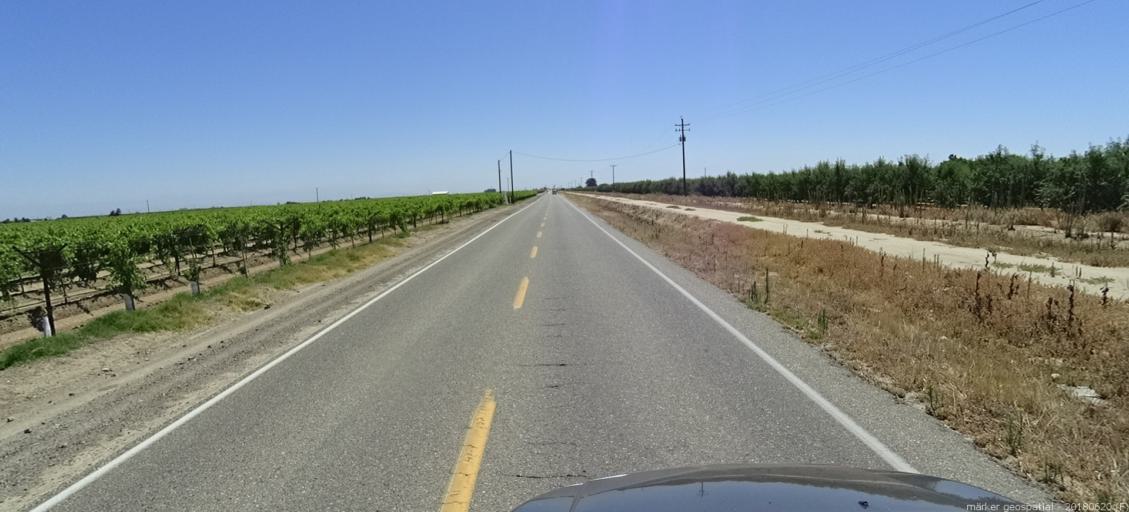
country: US
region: California
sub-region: Fresno County
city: Biola
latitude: 36.8512
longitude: -119.9821
